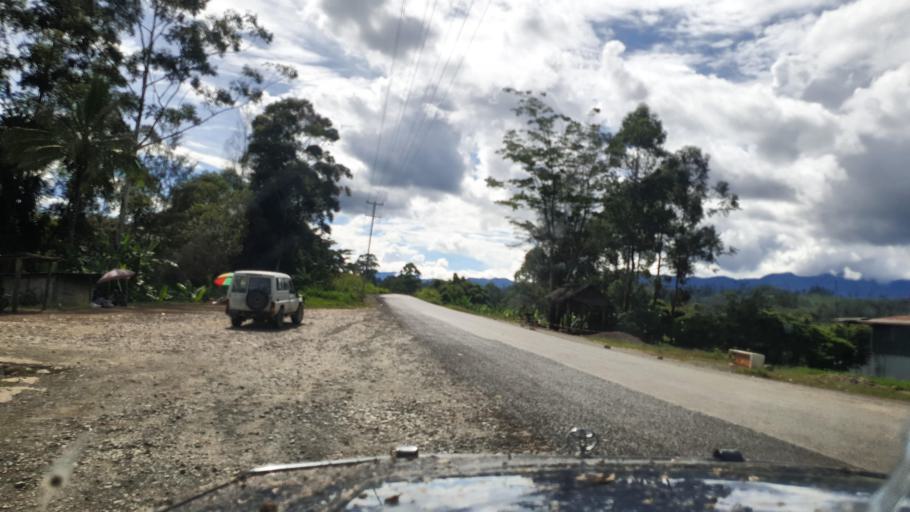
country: PG
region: Jiwaka
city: Minj
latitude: -5.8785
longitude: 144.7183
